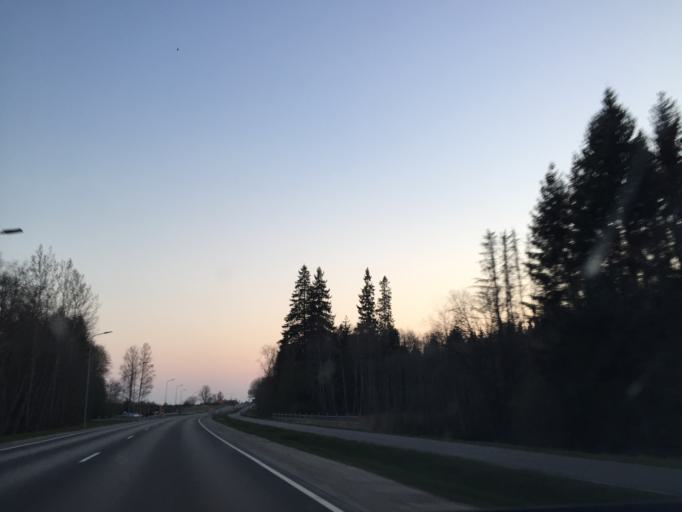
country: LV
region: Valkas Rajons
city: Valka
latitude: 57.7611
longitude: 25.9964
